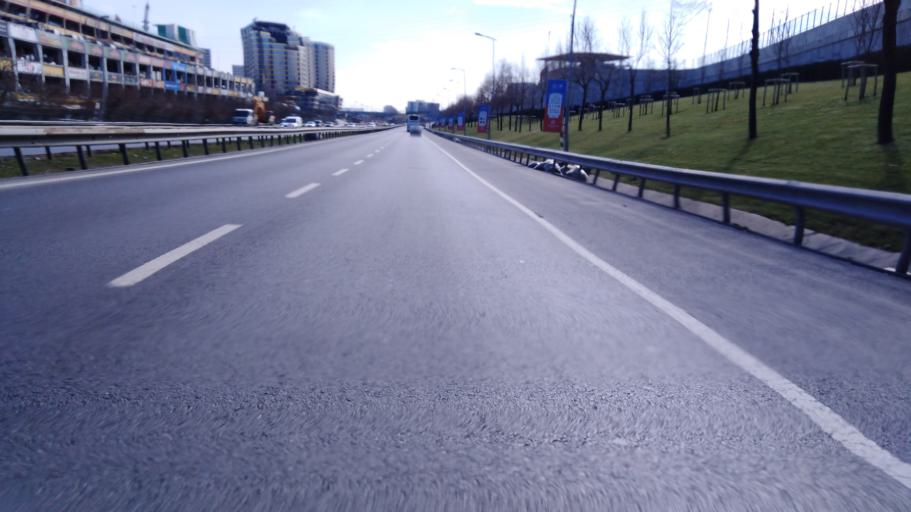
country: TR
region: Istanbul
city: Esenler
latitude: 41.0521
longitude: 28.8894
